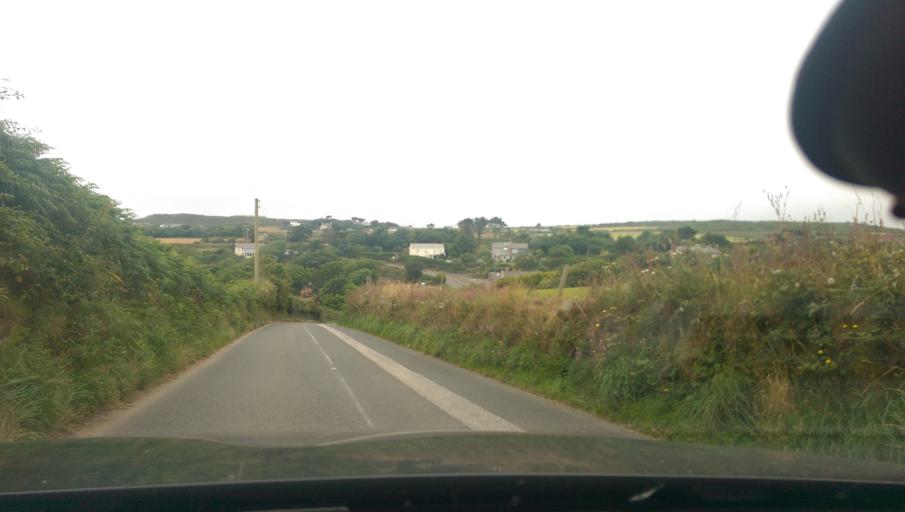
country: GB
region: England
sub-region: Cornwall
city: Saint Just
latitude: 50.1115
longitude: -5.6783
